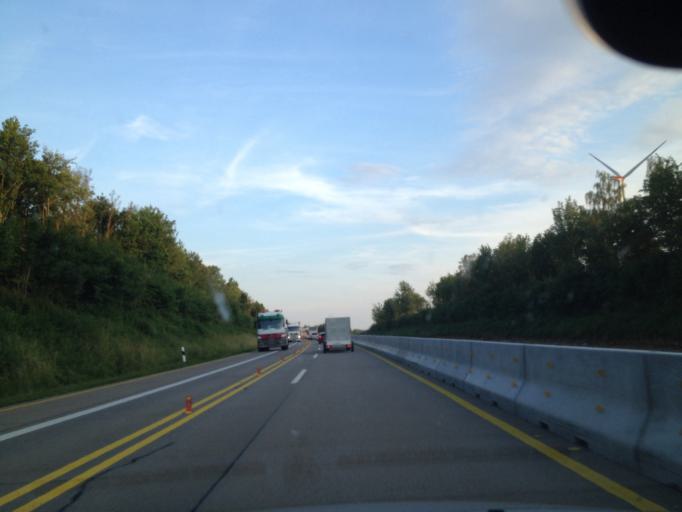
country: DE
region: Bavaria
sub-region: Regierungsbezirk Mittelfranken
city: Gollhofen
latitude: 49.5522
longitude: 10.1632
